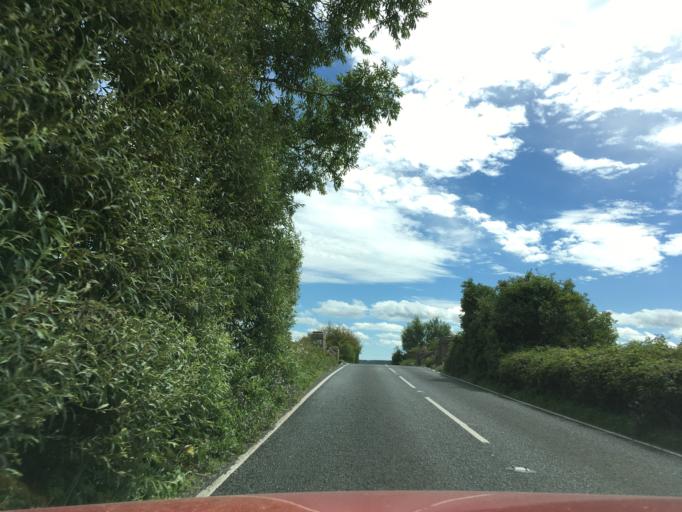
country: GB
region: England
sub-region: Somerset
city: Glastonbury
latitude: 51.1352
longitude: -2.7130
